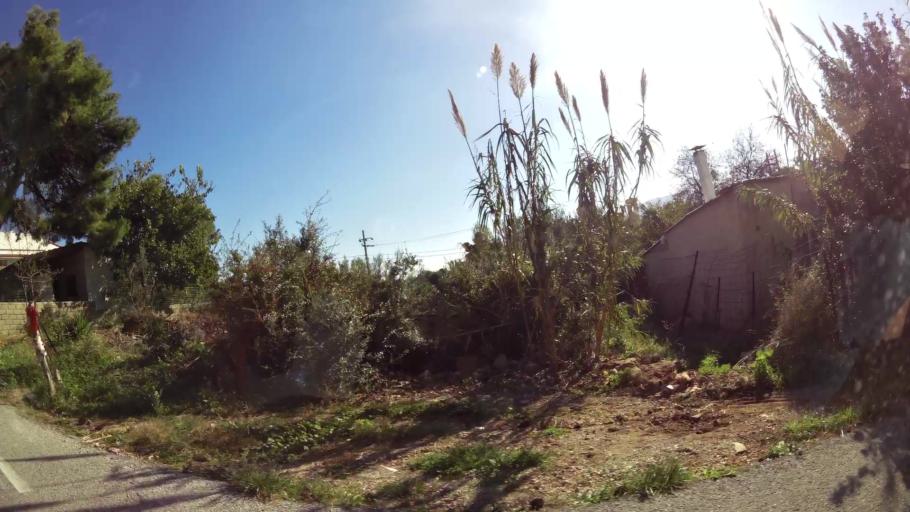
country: GR
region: Attica
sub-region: Nomarchia Anatolikis Attikis
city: Anthousa
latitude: 38.0274
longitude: 23.8741
